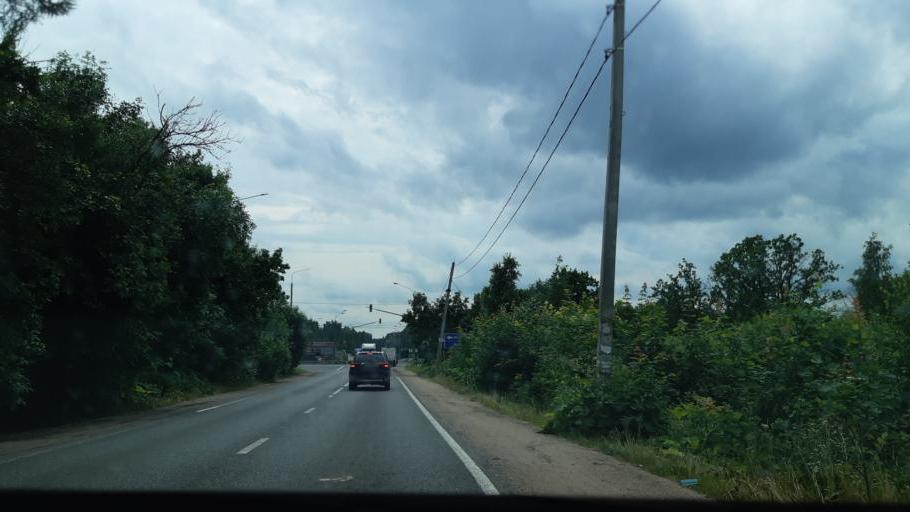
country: RU
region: Moskovskaya
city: Dorokhovo
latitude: 55.5323
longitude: 36.3602
